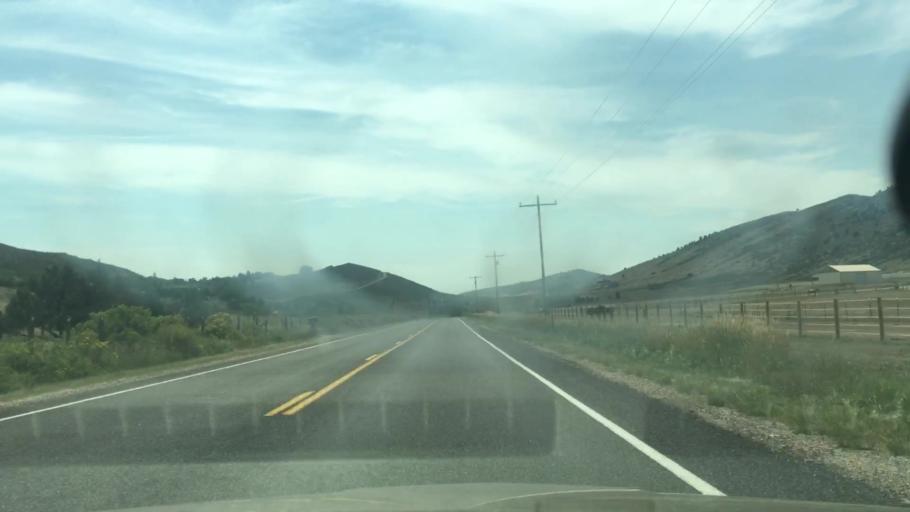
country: US
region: Colorado
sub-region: Larimer County
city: Campion
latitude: 40.3445
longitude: -105.1839
